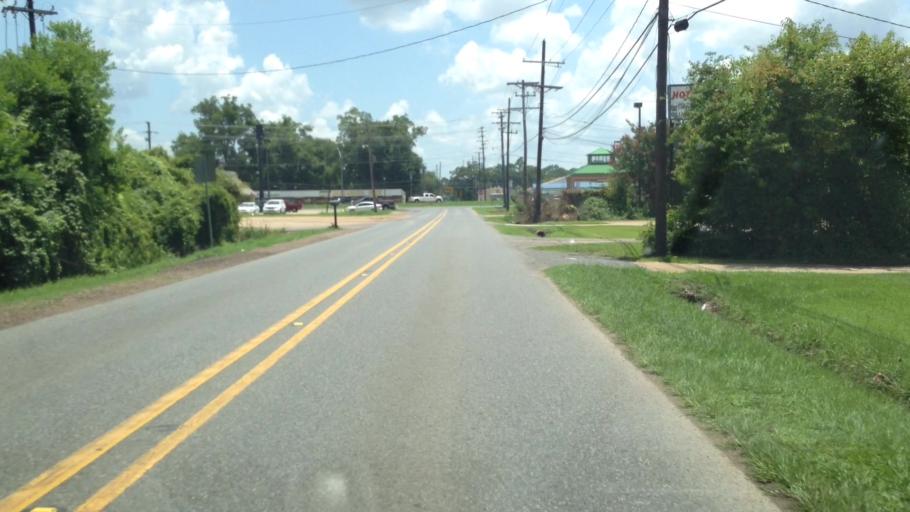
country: US
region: Louisiana
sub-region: Rapides Parish
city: Alexandria
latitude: 31.3119
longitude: -92.4792
